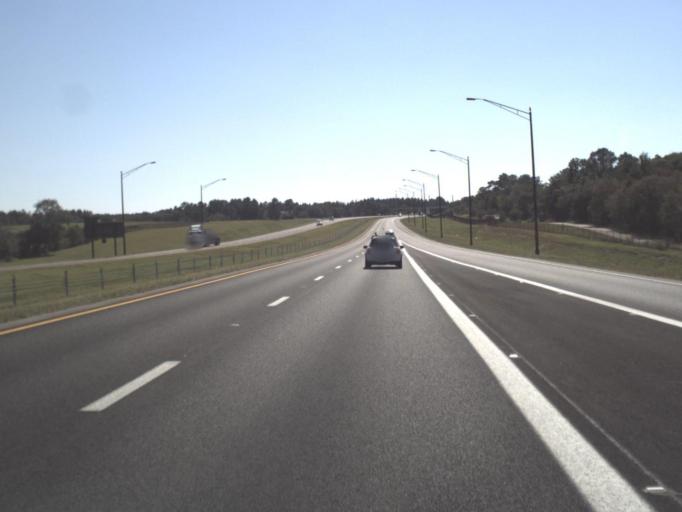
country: US
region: Florida
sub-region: Hernando County
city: Masaryktown
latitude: 28.4785
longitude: -82.4812
